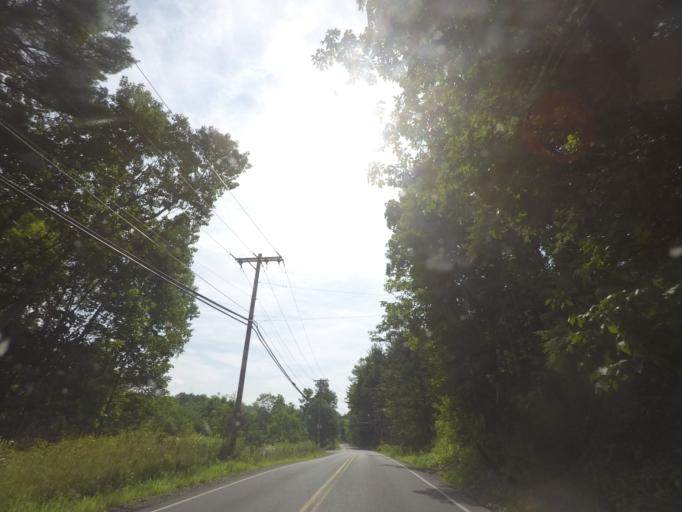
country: US
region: New York
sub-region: Rensselaer County
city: Wynantskill
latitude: 42.7045
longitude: -73.6137
